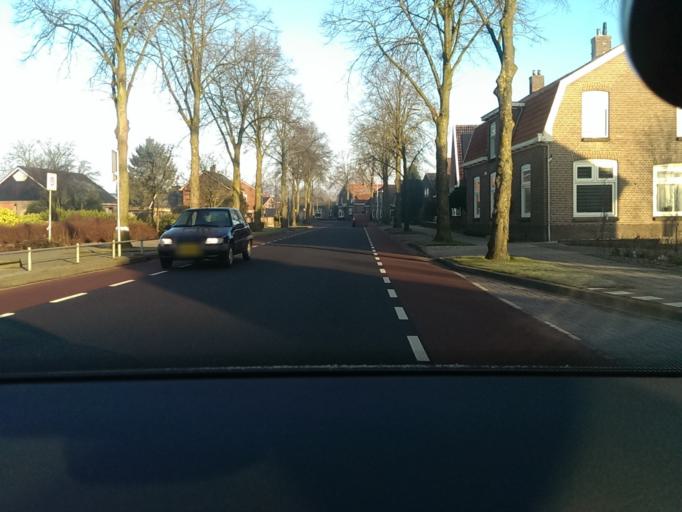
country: NL
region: Overijssel
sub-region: Gemeente Twenterand
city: Den Ham
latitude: 52.4637
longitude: 6.4874
